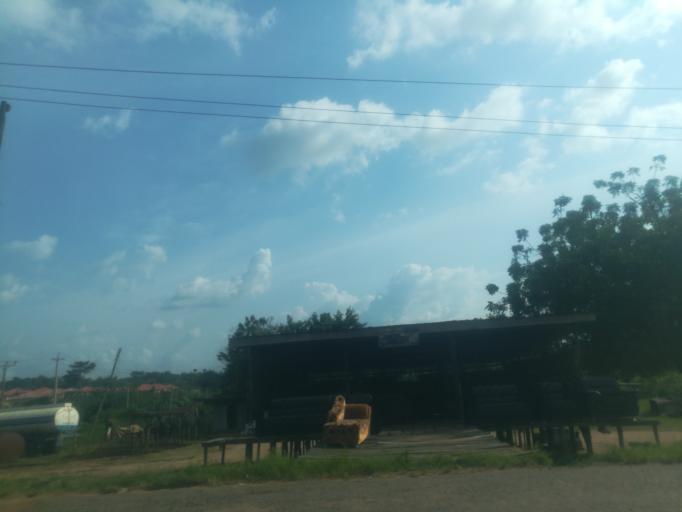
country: NG
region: Oyo
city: Ido
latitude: 7.3965
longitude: 3.7922
